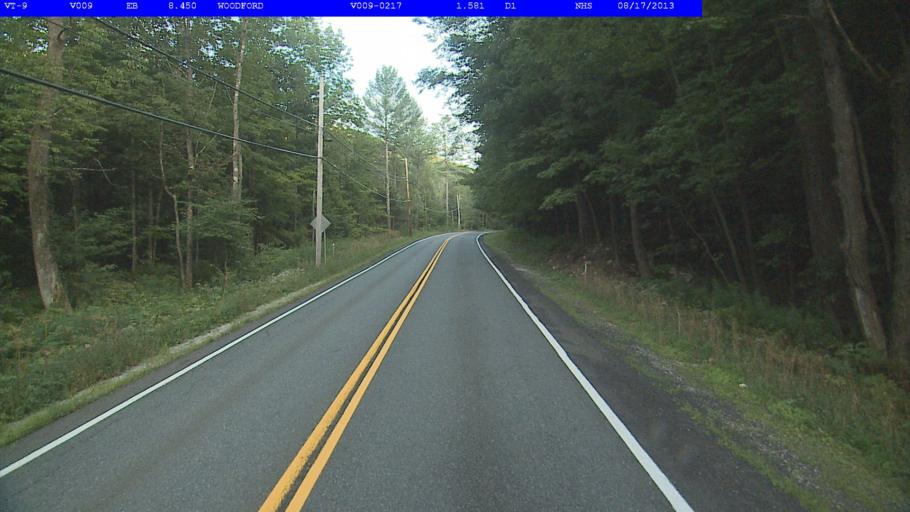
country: US
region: Vermont
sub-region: Bennington County
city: Bennington
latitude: 42.8953
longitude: -73.1269
